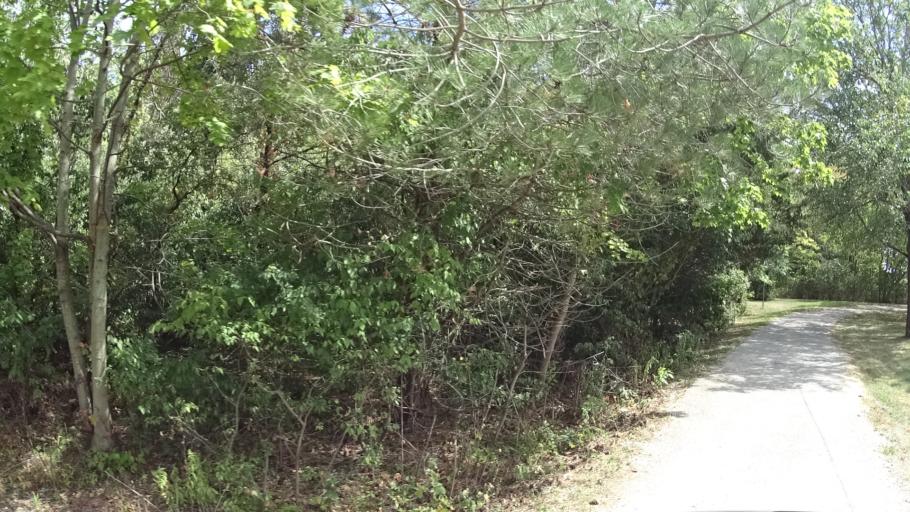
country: US
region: Ohio
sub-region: Erie County
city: Sandusky
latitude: 41.5972
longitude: -82.6789
